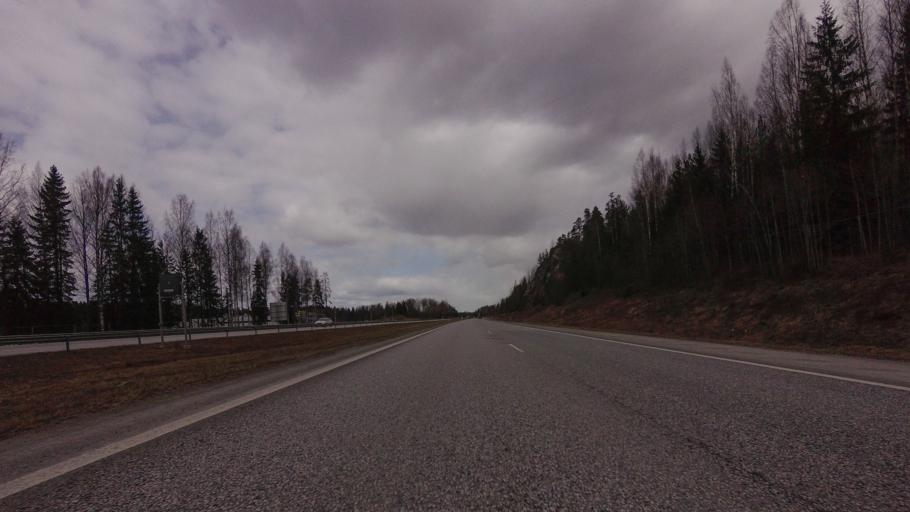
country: FI
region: Uusimaa
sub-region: Helsinki
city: Nurmijaervi
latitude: 60.3676
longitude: 24.8102
